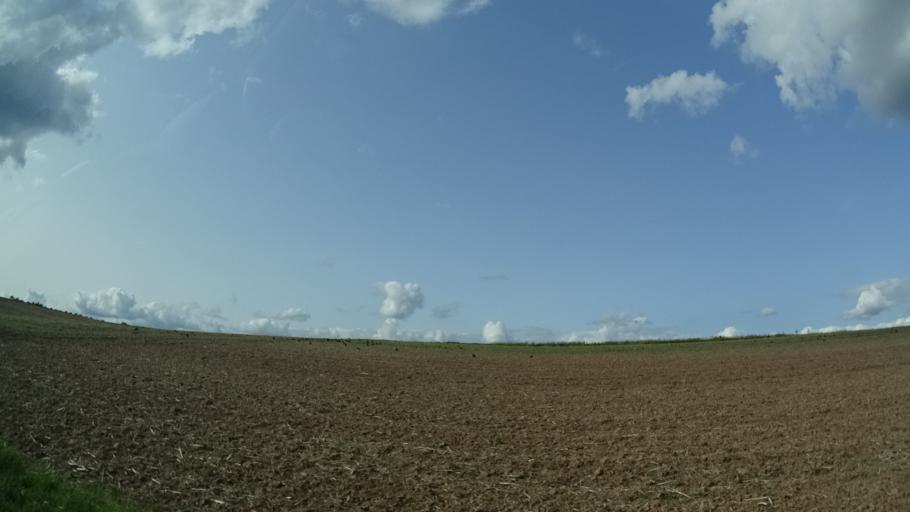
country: DE
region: Baden-Wuerttemberg
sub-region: Regierungsbezirk Stuttgart
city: Werbach
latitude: 49.6790
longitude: 9.5826
